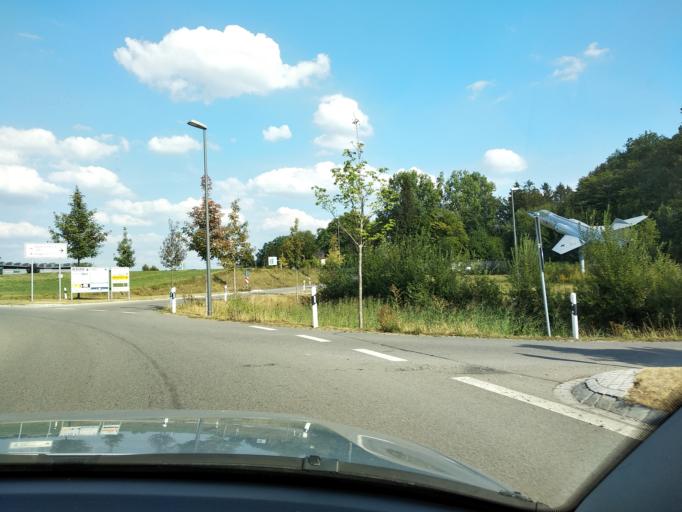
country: DE
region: Bavaria
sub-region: Swabia
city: Memmingerberg
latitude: 47.9910
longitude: 10.2176
